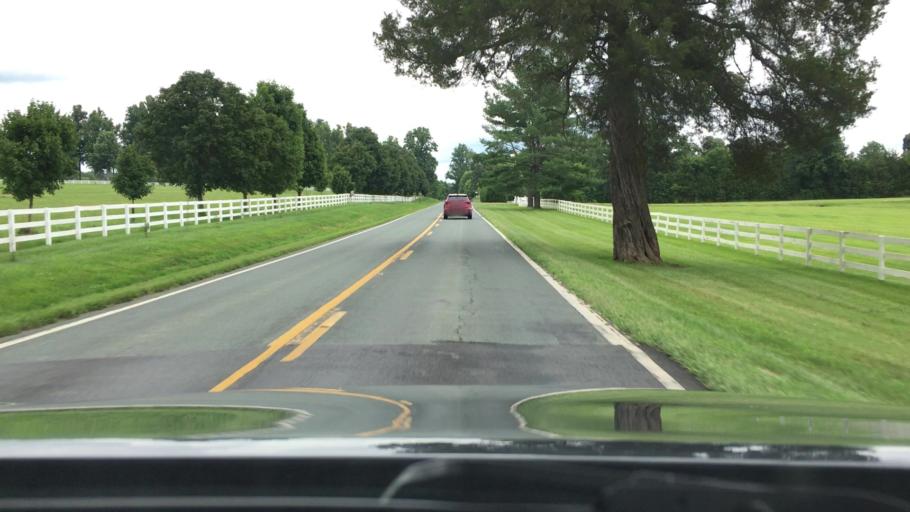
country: US
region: Virginia
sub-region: Orange County
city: Gordonsville
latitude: 38.0782
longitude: -78.2912
